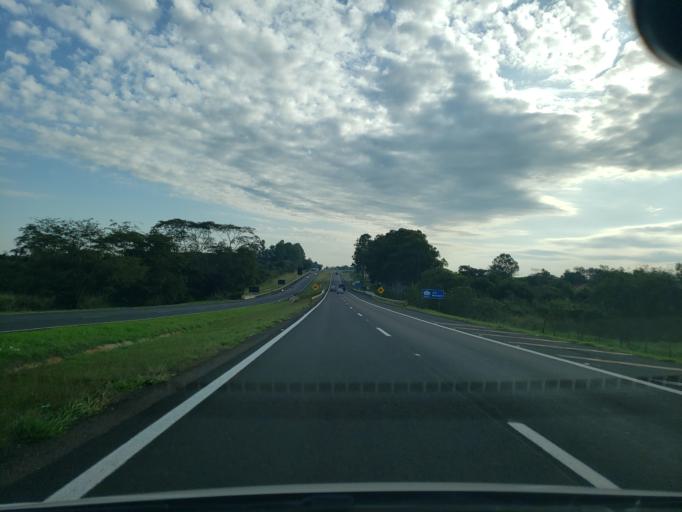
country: BR
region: Sao Paulo
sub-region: Guararapes
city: Guararapes
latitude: -21.2075
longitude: -50.6497
